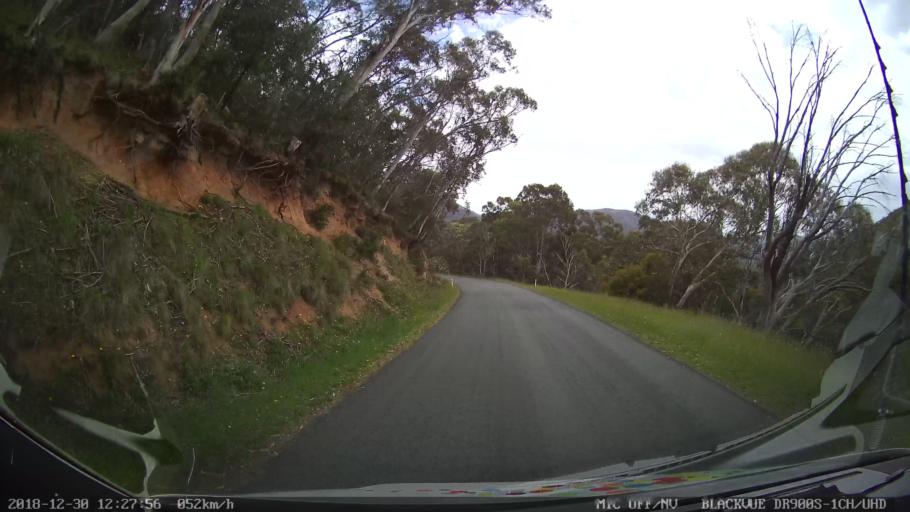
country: AU
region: New South Wales
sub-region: Snowy River
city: Jindabyne
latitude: -36.3276
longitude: 148.4886
